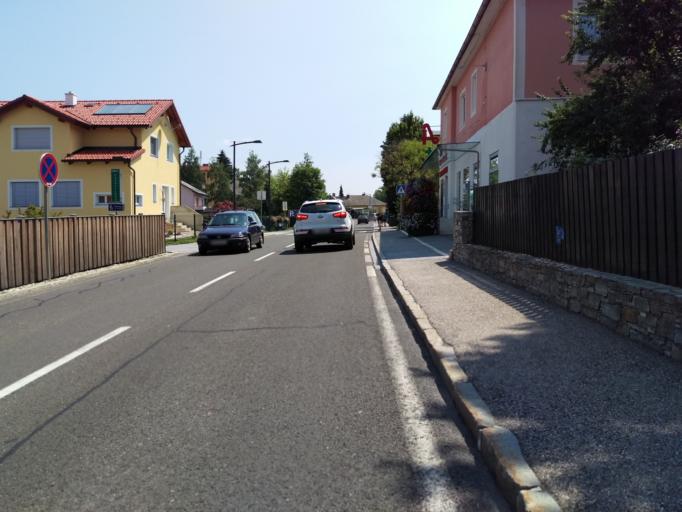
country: AT
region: Styria
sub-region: Politischer Bezirk Graz-Umgebung
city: Nestelbach bei Graz
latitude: 47.0752
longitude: 15.5883
